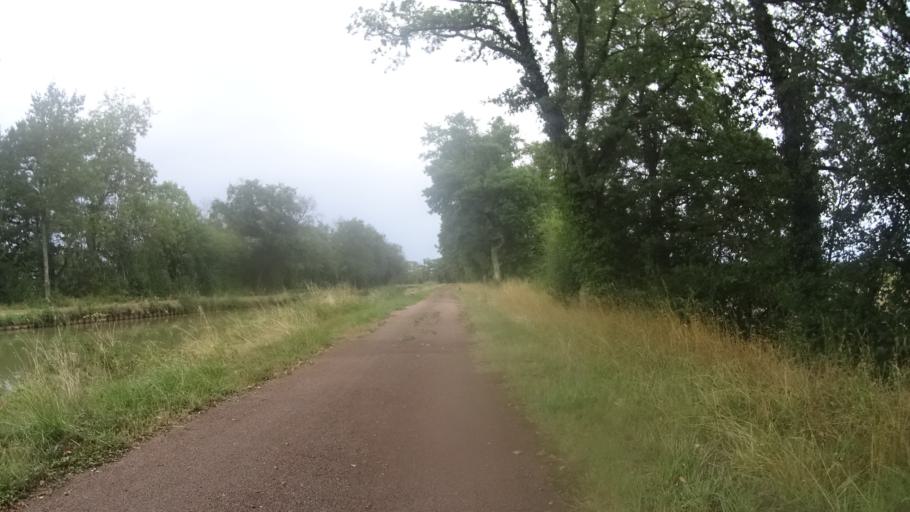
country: FR
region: Bourgogne
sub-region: Departement de la Nievre
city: Imphy
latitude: 46.9040
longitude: 3.2470
